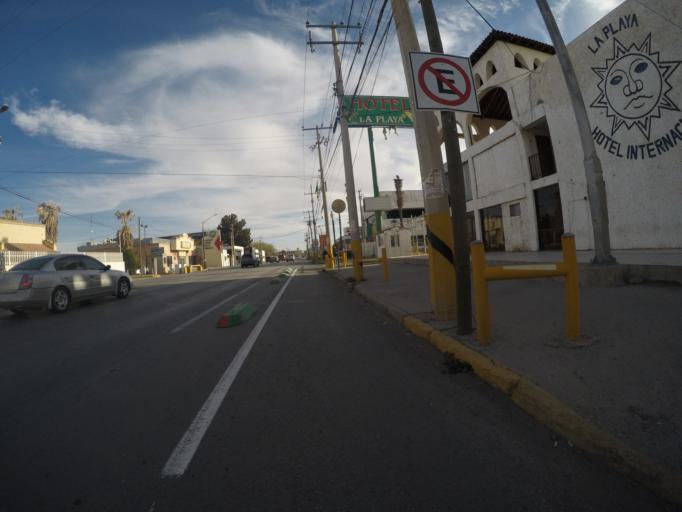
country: MX
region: Chihuahua
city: Ciudad Juarez
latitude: 31.7461
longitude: -106.4488
